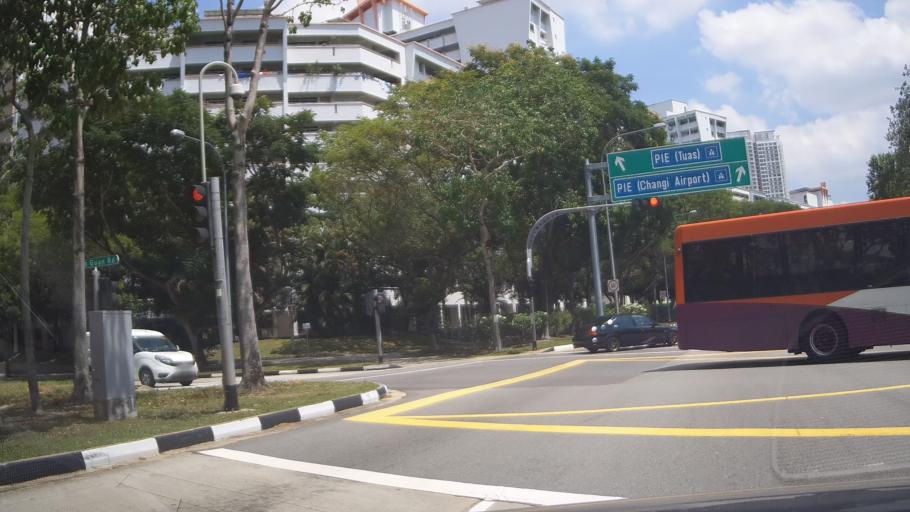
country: SG
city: Singapore
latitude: 1.3384
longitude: 103.7475
